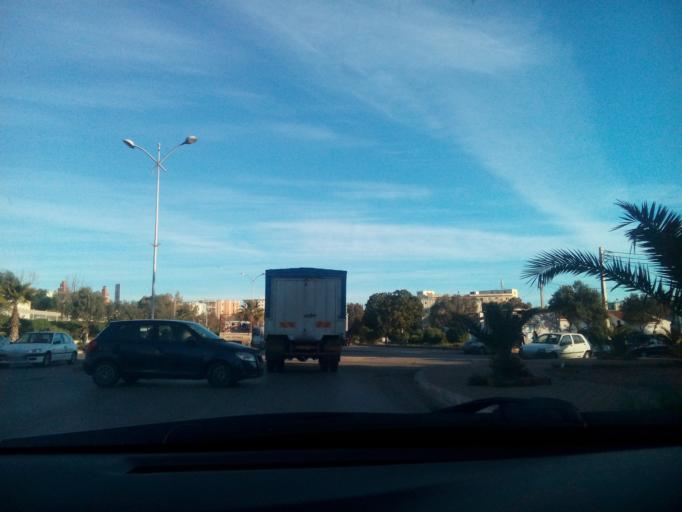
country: DZ
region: Oran
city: Oran
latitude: 35.6684
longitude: -0.6642
